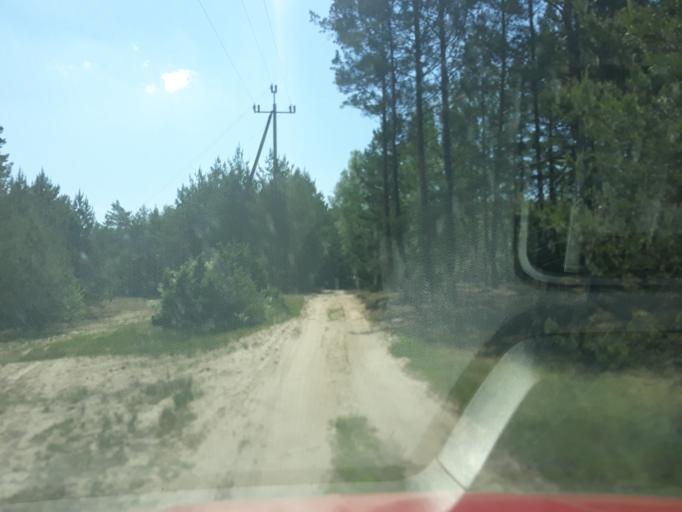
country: PL
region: Pomeranian Voivodeship
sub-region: Powiat chojnicki
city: Chojnice
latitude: 53.8715
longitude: 17.5401
